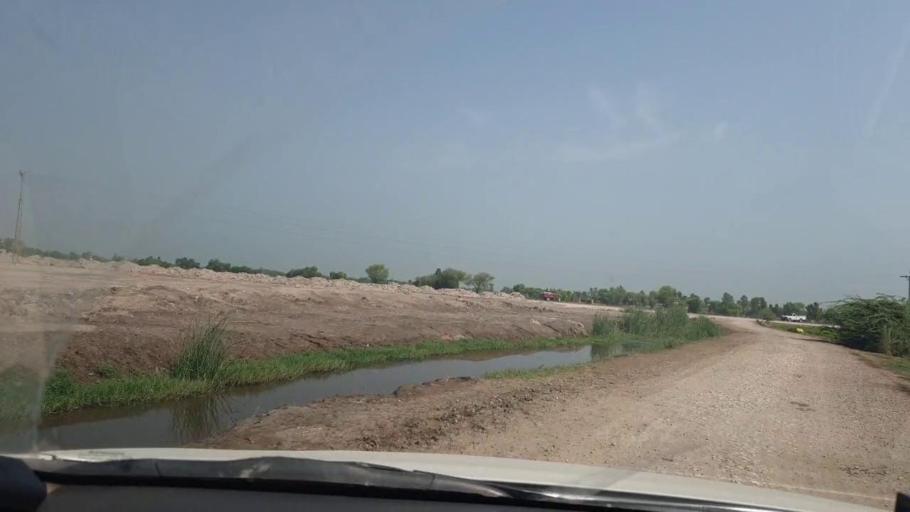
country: PK
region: Sindh
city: Chak
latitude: 27.8409
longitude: 68.7985
